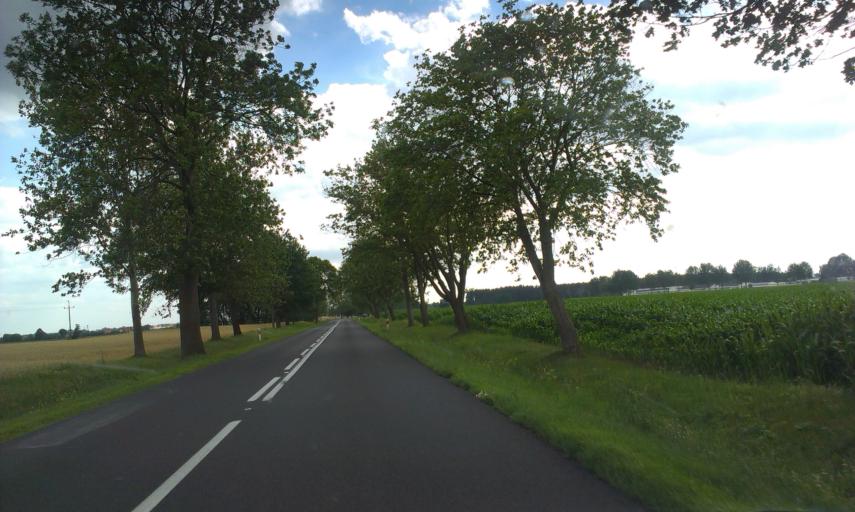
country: PL
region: Greater Poland Voivodeship
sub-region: Powiat zlotowski
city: Krajenka
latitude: 53.3243
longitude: 16.9995
